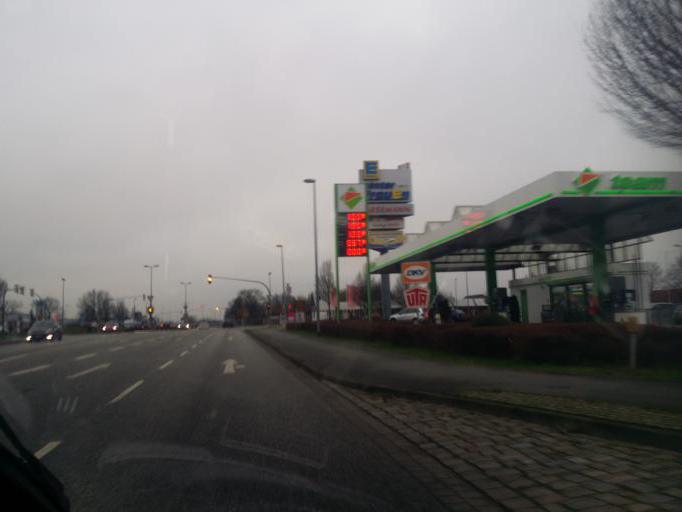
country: DE
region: Schleswig-Holstein
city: Heide
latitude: 54.1986
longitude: 9.1245
